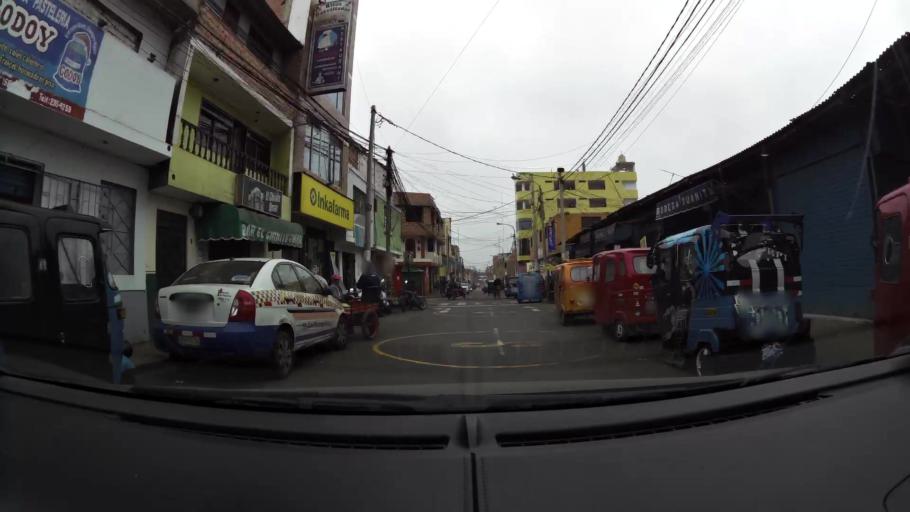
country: PE
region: Lima
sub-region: Barranca
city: Barranca
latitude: -10.7531
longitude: -77.7612
